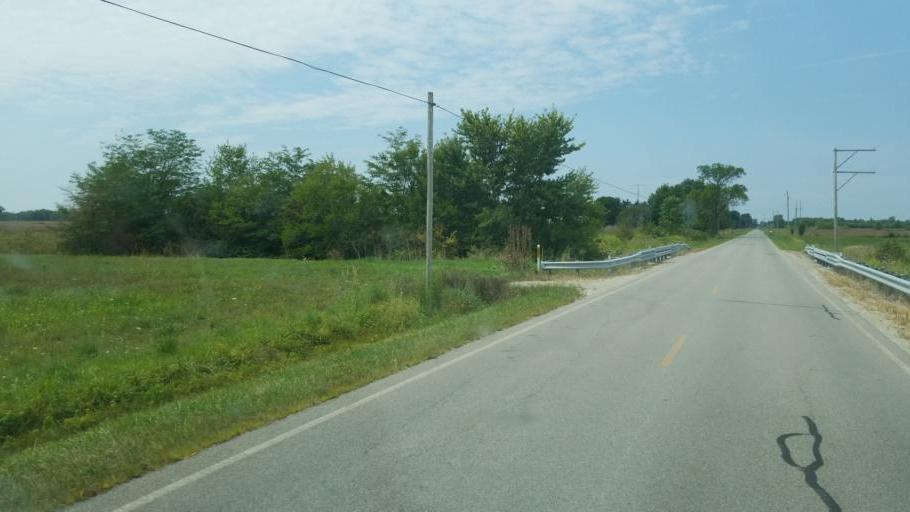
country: US
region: Ohio
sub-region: Marion County
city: Marion
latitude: 40.5714
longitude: -83.1783
